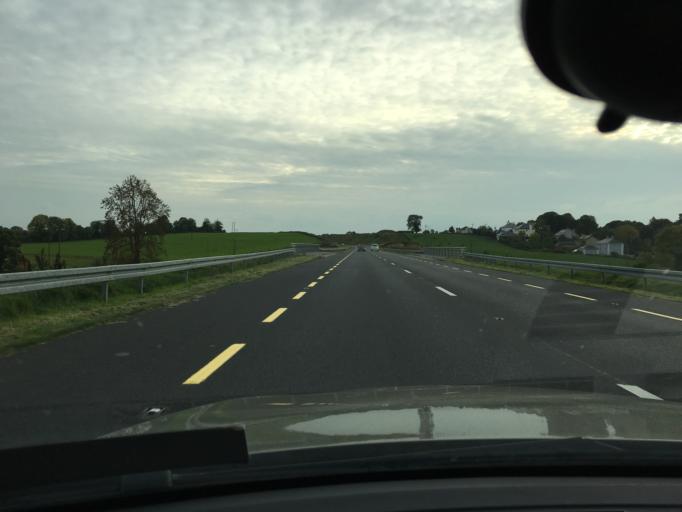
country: IE
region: Leinster
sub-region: An Longfort
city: Longford
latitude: 53.7334
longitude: -7.8210
